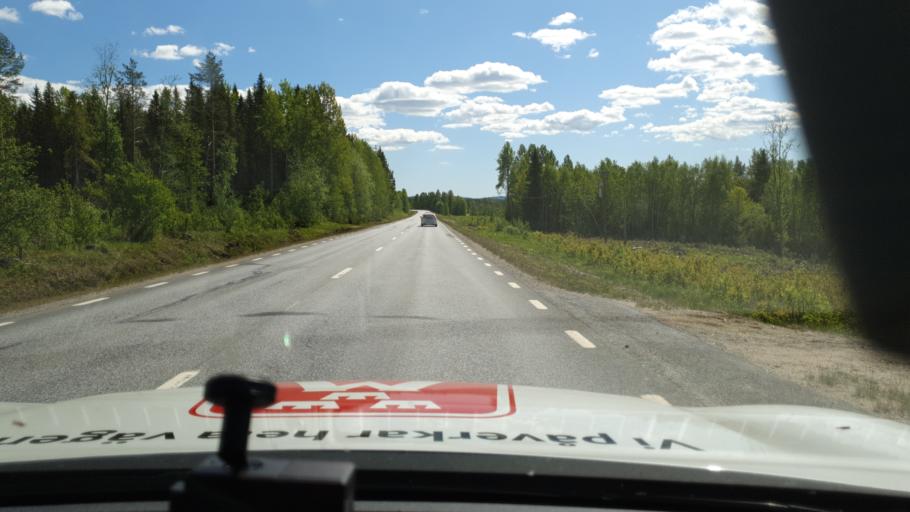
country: SE
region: Vaesterbotten
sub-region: Vannas Kommun
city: Vaennaes
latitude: 63.9742
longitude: 19.7346
